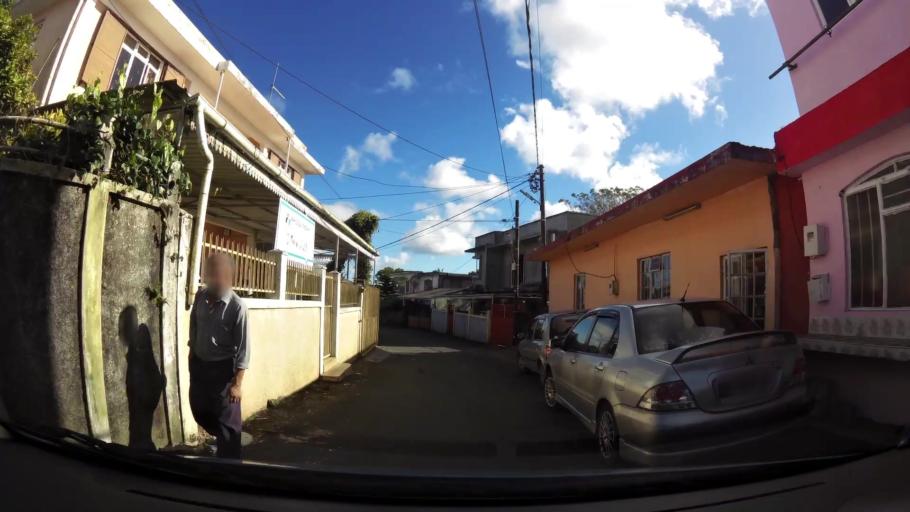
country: MU
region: Plaines Wilhems
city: Curepipe
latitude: -20.3014
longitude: 57.5194
